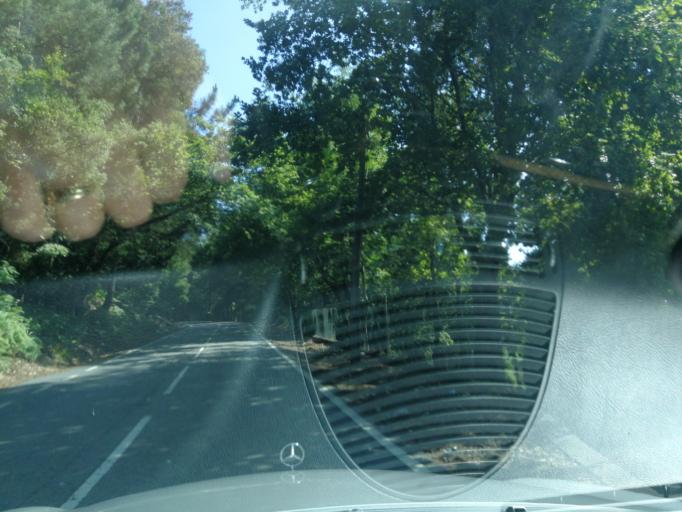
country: PT
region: Braga
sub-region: Braga
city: Adaufe
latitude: 41.5780
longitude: -8.3880
